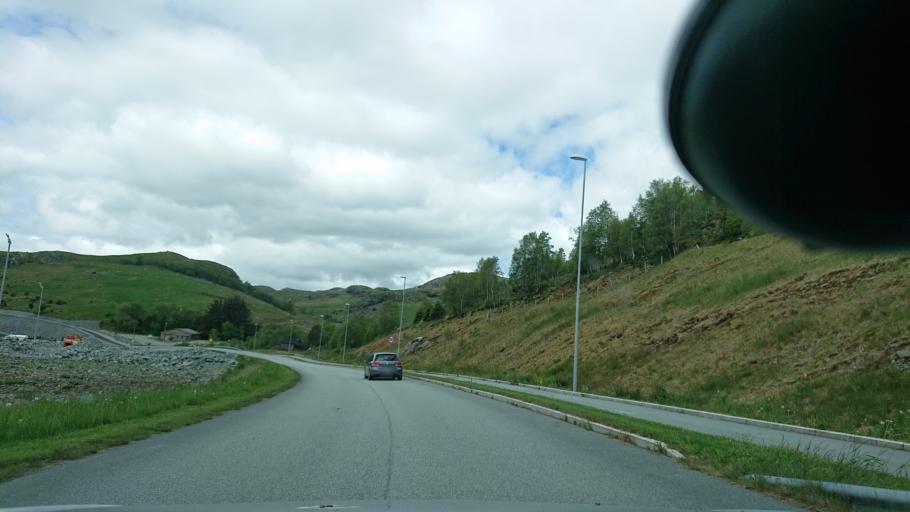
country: NO
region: Rogaland
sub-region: Gjesdal
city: Algard
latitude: 58.7760
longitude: 5.8710
